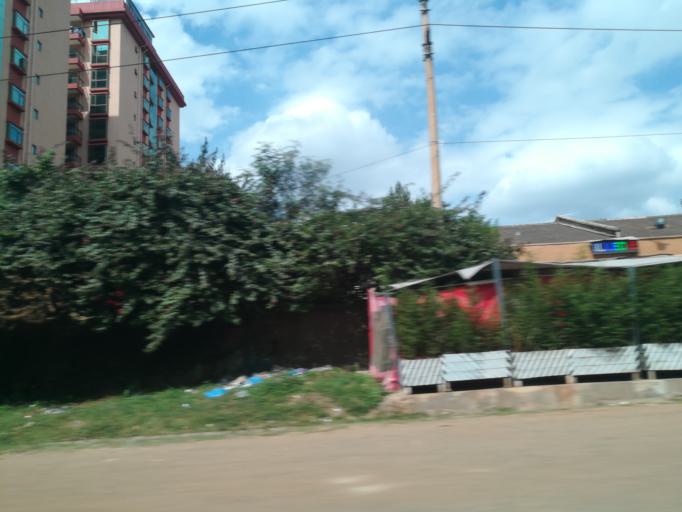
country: KE
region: Nairobi Area
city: Nairobi
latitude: -1.2882
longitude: 36.7873
